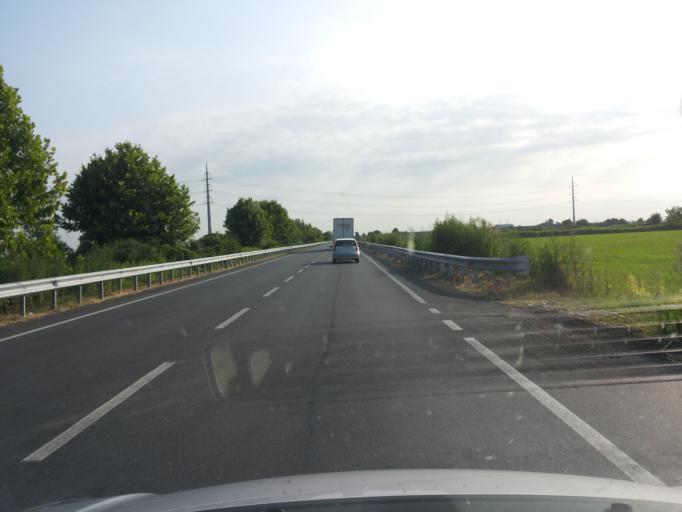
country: IT
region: Piedmont
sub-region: Provincia di Vercelli
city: Desana
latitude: 45.2824
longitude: 8.3721
